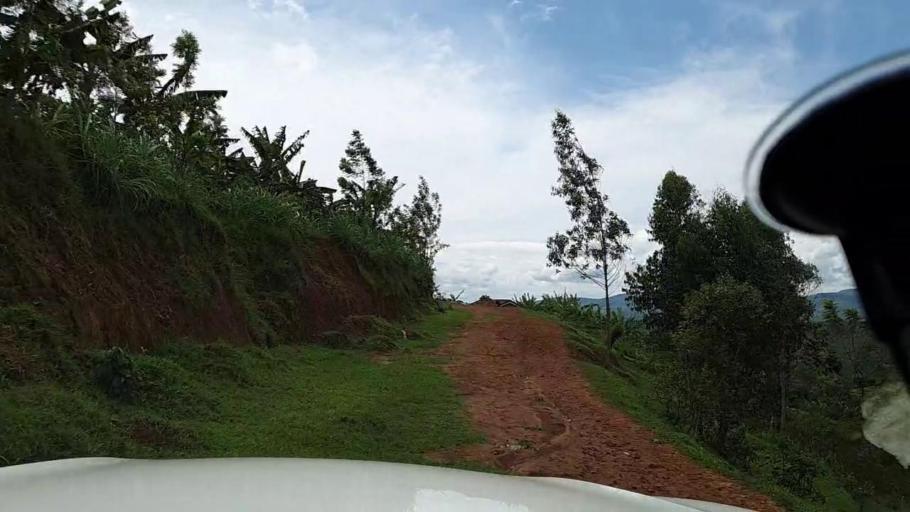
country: RW
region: Southern Province
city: Gitarama
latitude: -2.0665
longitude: 29.6451
